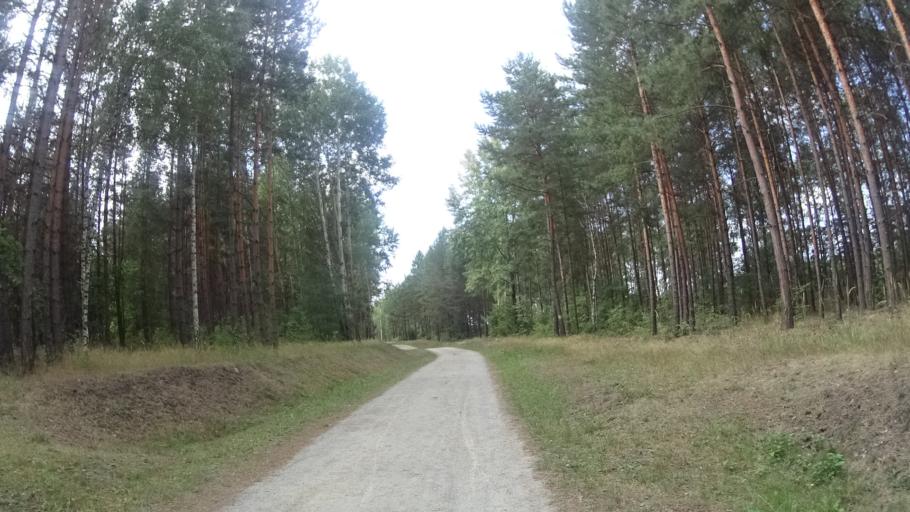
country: PL
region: Lubusz
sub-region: Powiat zarski
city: Leknica
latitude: 51.5373
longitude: 14.7761
